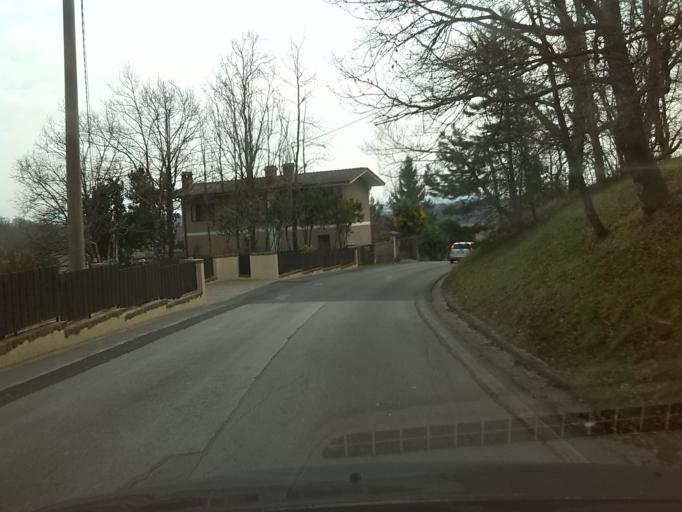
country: IT
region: Friuli Venezia Giulia
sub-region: Provincia di Gorizia
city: Mossa
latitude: 45.9651
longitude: 13.5552
